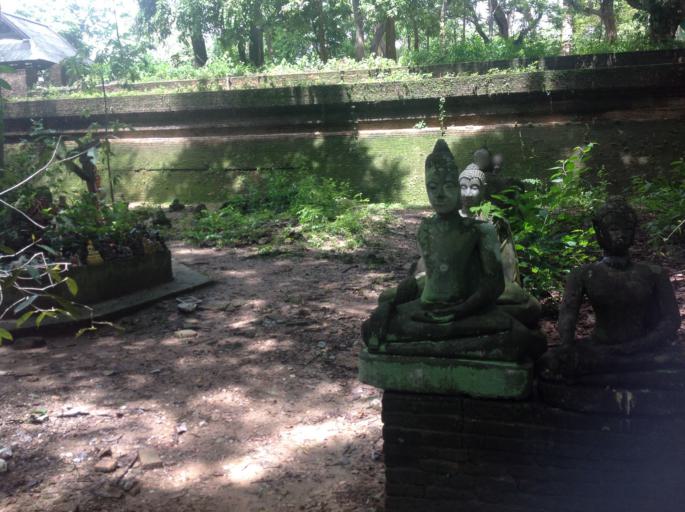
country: TH
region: Chiang Mai
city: Chiang Mai
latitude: 18.7837
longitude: 98.9519
